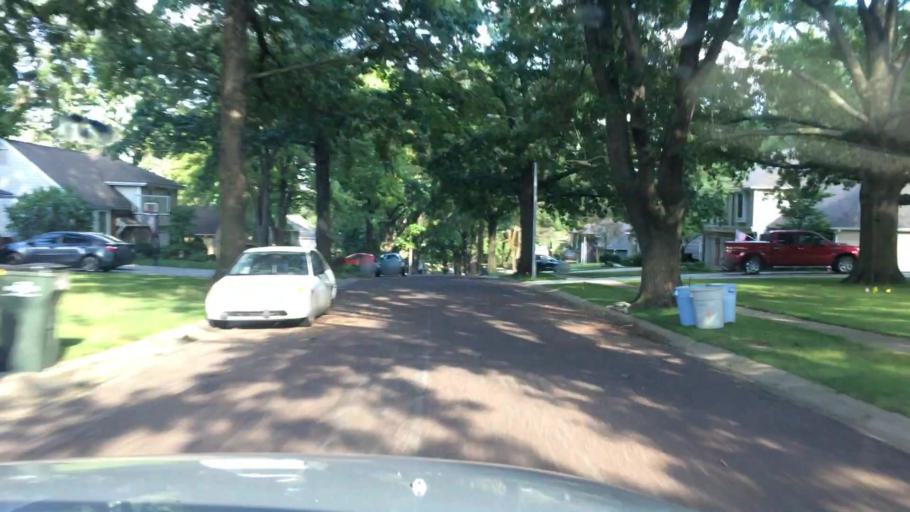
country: US
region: Kansas
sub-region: Johnson County
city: Overland Park
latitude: 38.9668
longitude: -94.6570
